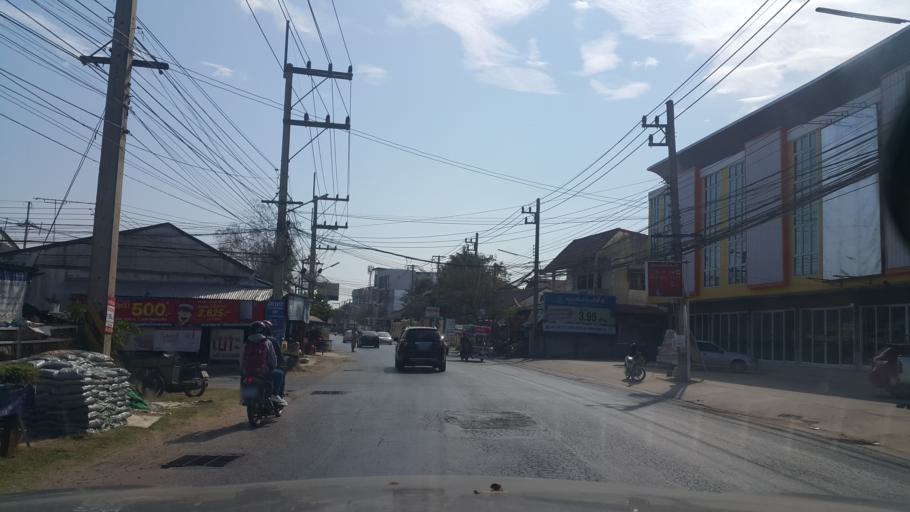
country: TH
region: Nakhon Ratchasima
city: Nakhon Ratchasima
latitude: 14.9481
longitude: 102.0497
